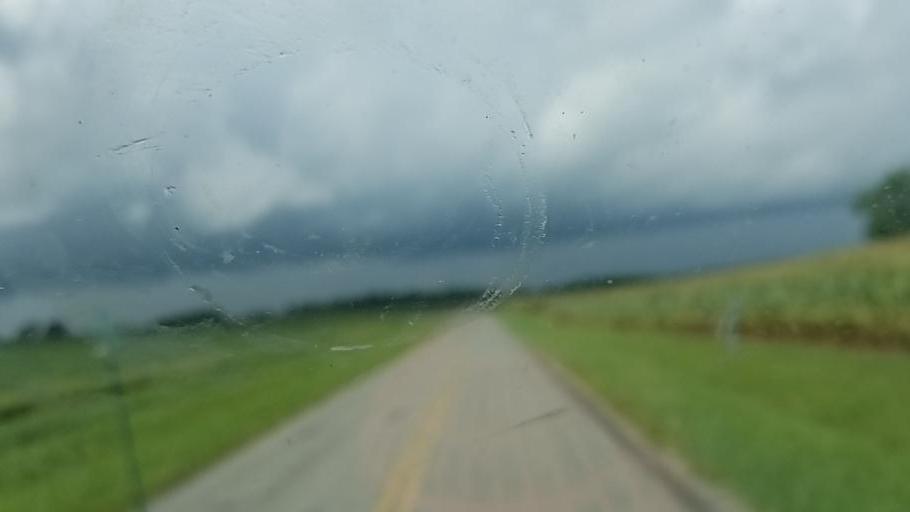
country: US
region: Ohio
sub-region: Champaign County
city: North Lewisburg
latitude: 40.2512
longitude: -83.6512
